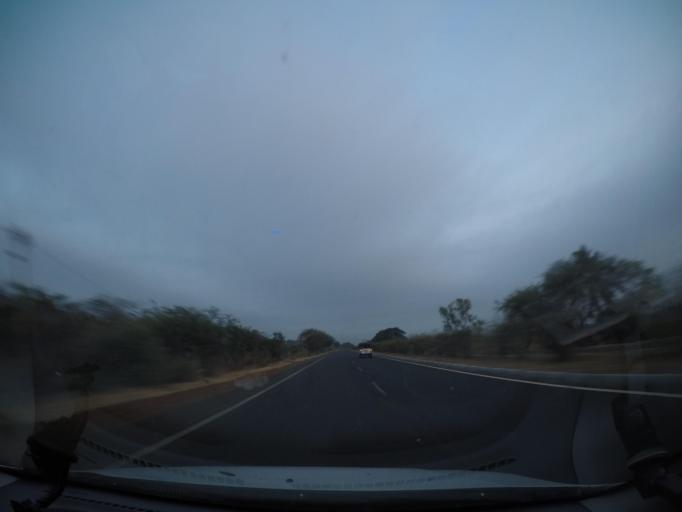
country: IN
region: Andhra Pradesh
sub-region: West Godavari
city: Tadepallegudem
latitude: 16.8098
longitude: 81.3587
